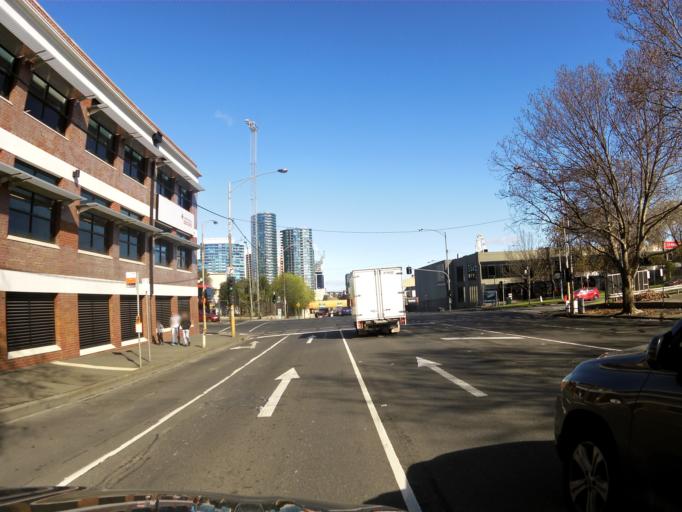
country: AU
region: Victoria
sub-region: Melbourne
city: West Melbourne
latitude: -37.8108
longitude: 144.9484
